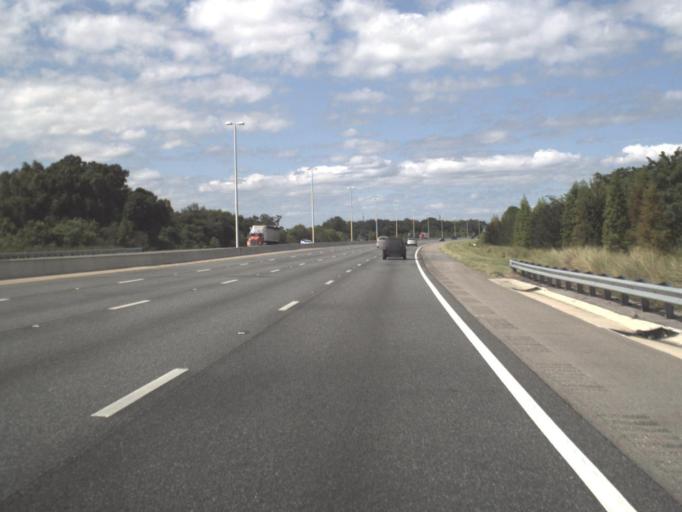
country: US
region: Florida
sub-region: Orange County
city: Oakland
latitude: 28.5455
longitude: -81.6137
